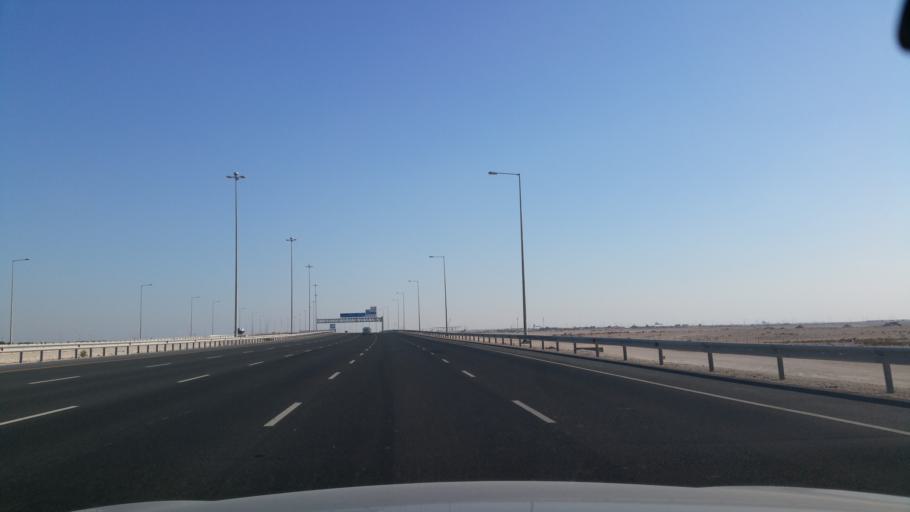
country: QA
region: Al Wakrah
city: Al Wukayr
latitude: 25.1391
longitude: 51.4765
